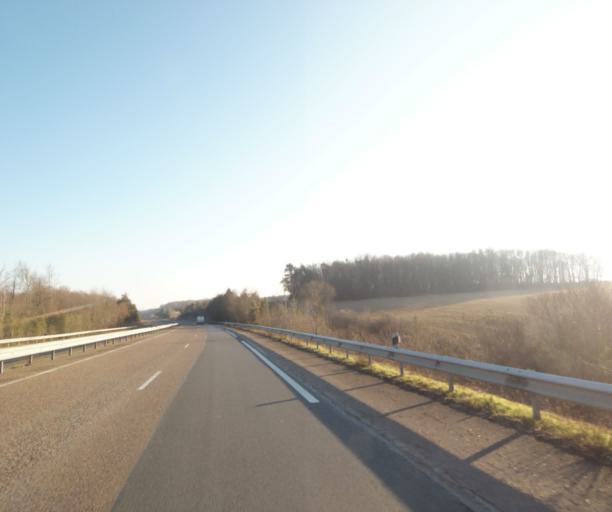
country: FR
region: Champagne-Ardenne
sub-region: Departement de la Haute-Marne
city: Chevillon
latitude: 48.5106
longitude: 5.0948
